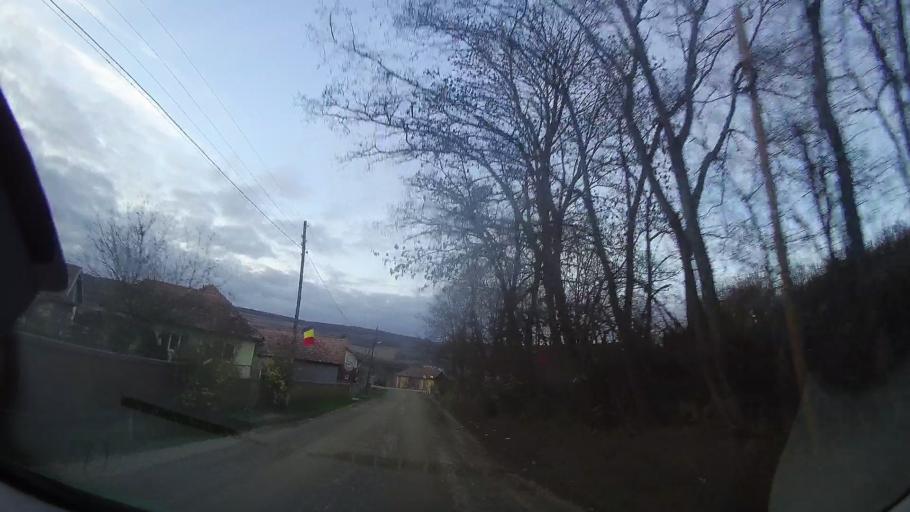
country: RO
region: Cluj
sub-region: Comuna Palatca
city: Palatca
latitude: 46.8684
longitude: 24.0139
